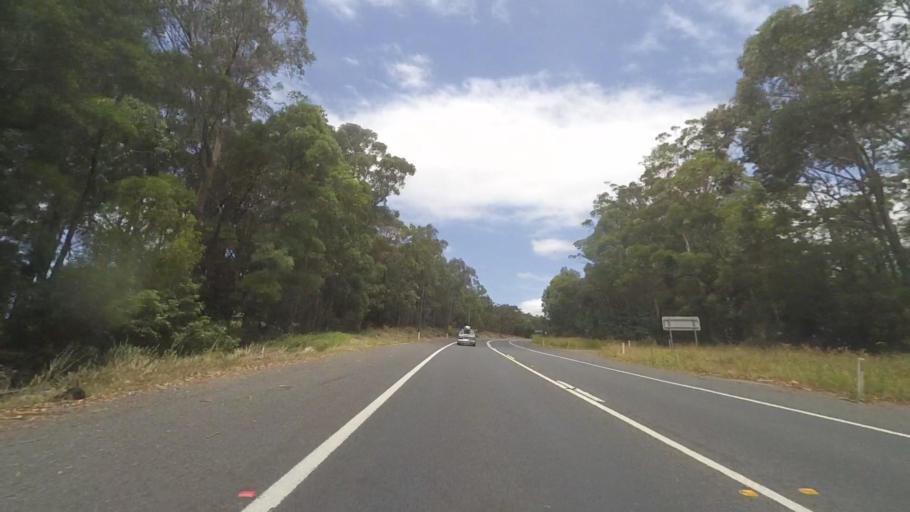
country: AU
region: New South Wales
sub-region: Shoalhaven Shire
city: Milton
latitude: -35.2287
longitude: 150.4351
